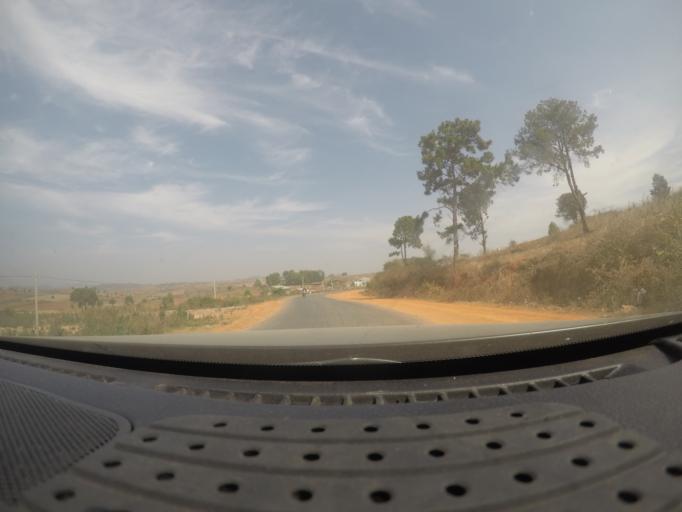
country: MM
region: Shan
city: Taunggyi
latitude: 20.7006
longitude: 96.6267
